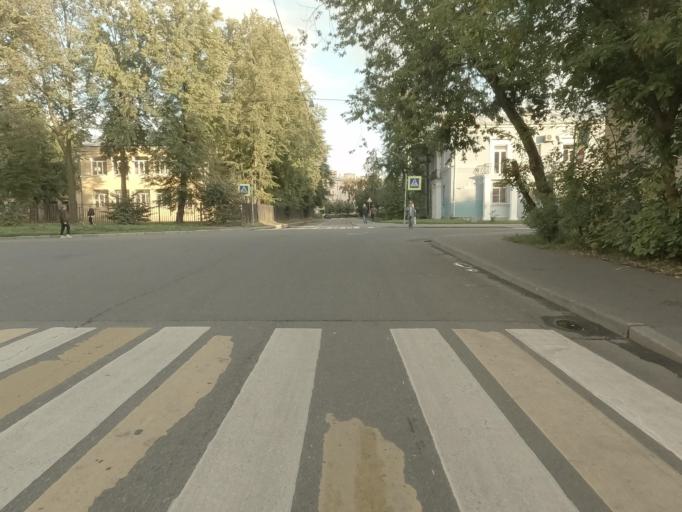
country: RU
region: St.-Petersburg
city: Admiralteisky
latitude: 59.8976
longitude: 30.2718
